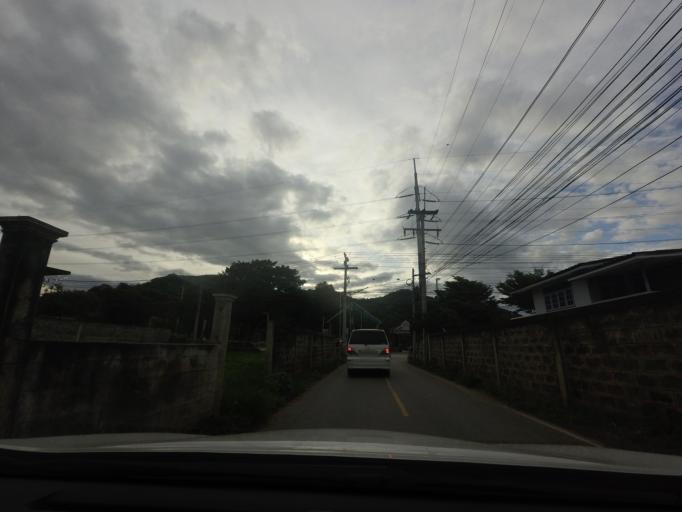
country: TH
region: Nakhon Ratchasima
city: Pak Chong
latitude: 14.6098
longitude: 101.4030
